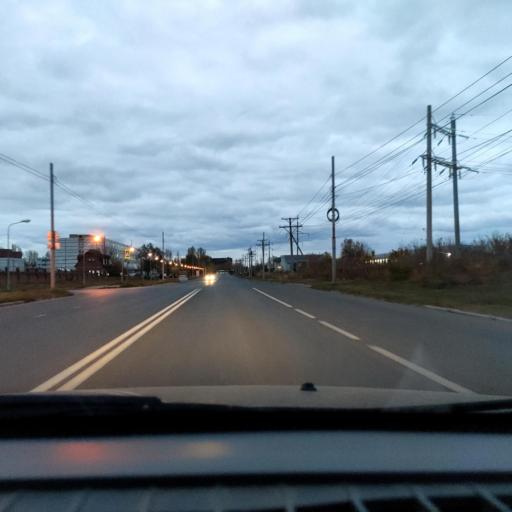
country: RU
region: Samara
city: Tol'yatti
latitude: 53.5573
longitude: 49.2943
